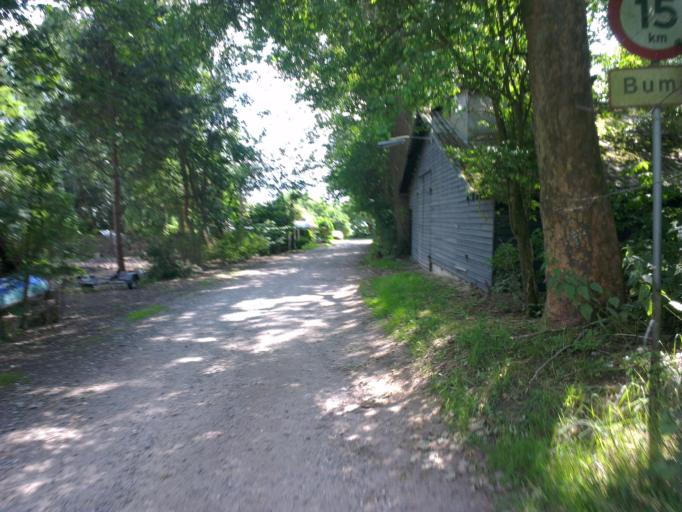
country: DK
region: Zealand
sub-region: Lejre Kommune
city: Ejby
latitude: 55.7378
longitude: 11.8624
